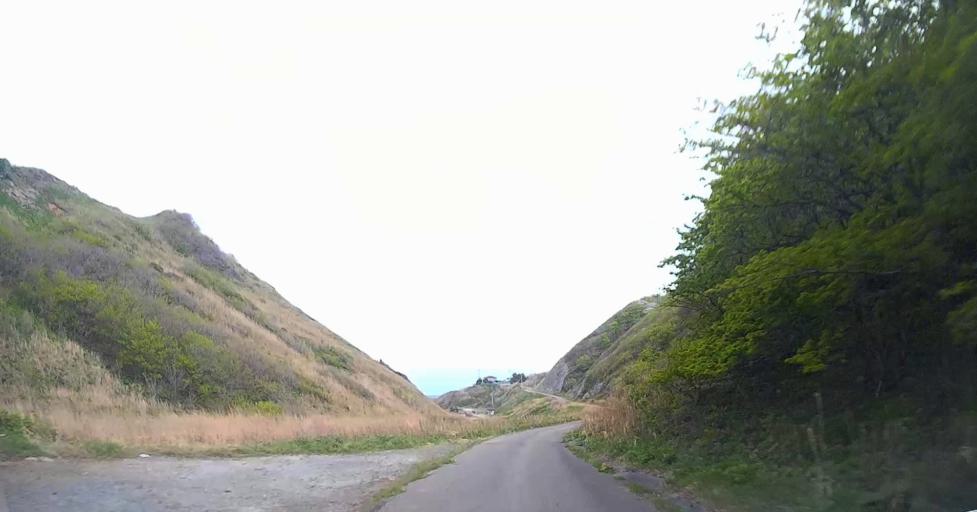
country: JP
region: Aomori
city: Shimokizukuri
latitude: 41.2399
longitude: 140.3436
